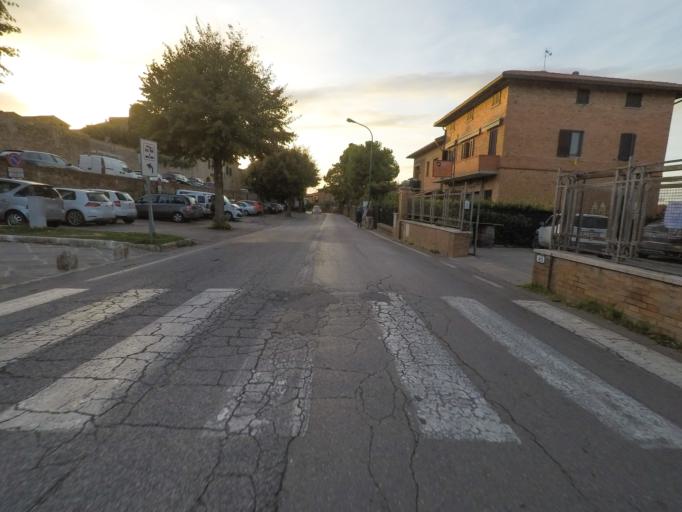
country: IT
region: Tuscany
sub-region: Provincia di Siena
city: Pienza
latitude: 43.0773
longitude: 11.6803
